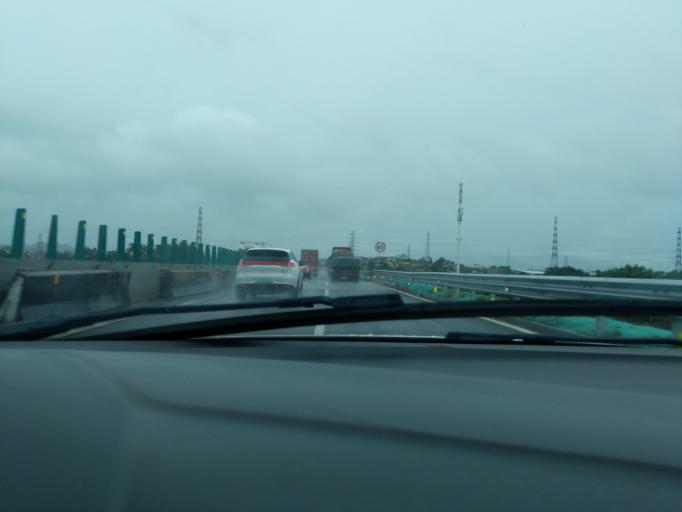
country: CN
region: Guangdong
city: Shuikou
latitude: 22.4684
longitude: 112.7571
